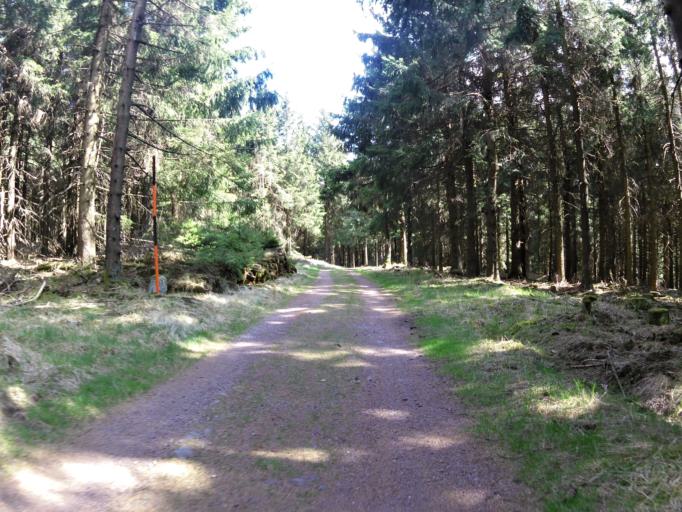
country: DE
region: Thuringia
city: Unterschonau
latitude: 50.7392
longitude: 10.5795
